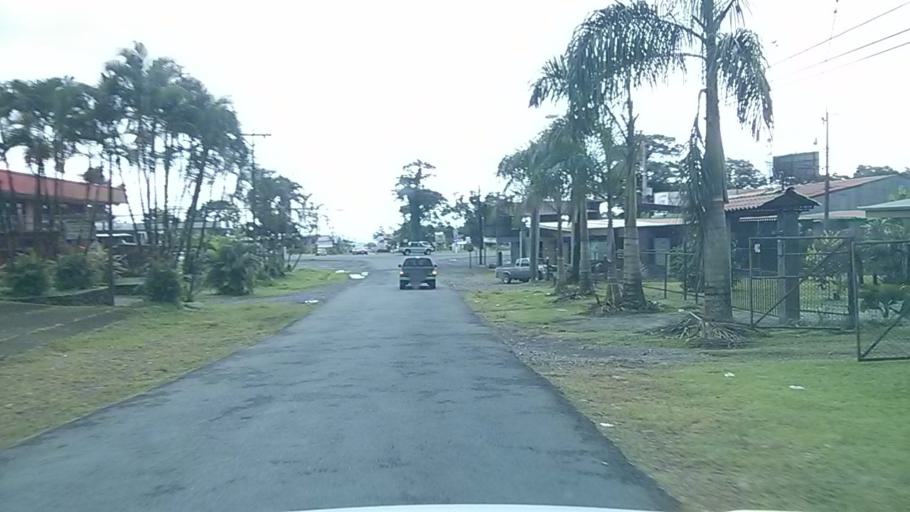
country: CR
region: Limon
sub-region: Canton de Pococi
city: Guapiles
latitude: 10.2018
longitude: -83.7818
